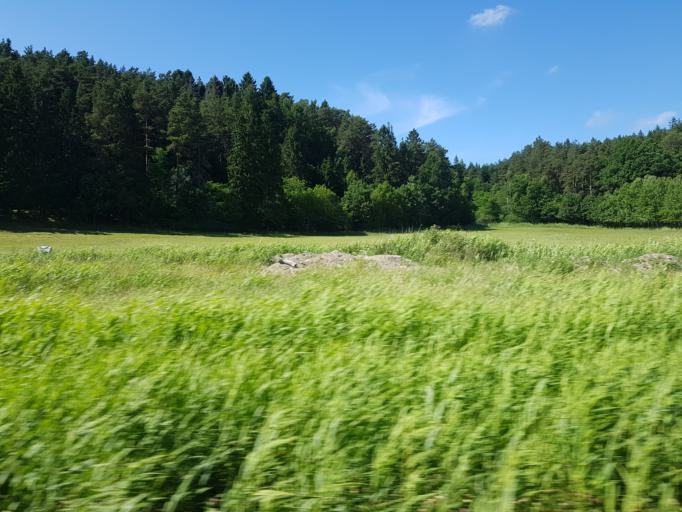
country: SE
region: Vaestra Goetaland
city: Ronnang
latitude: 57.9692
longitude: 11.6374
